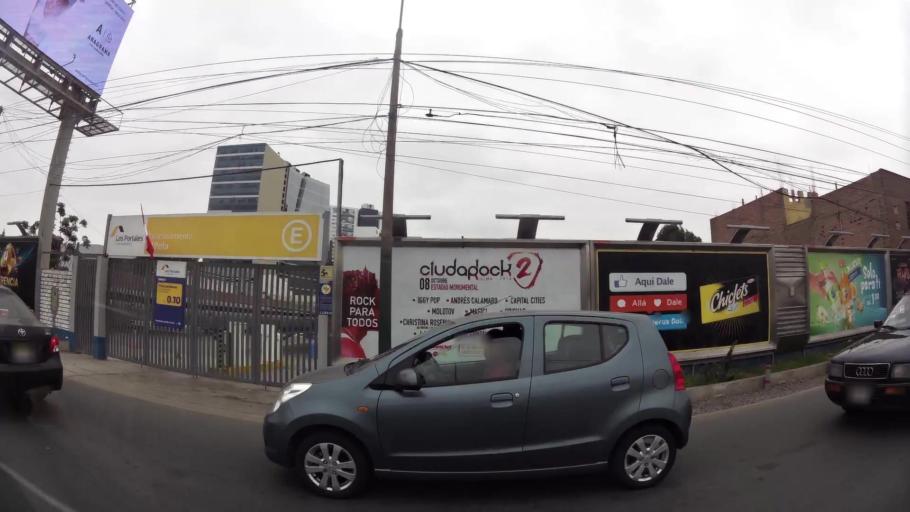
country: PE
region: Lima
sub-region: Lima
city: La Molina
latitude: -12.0975
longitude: -76.9706
